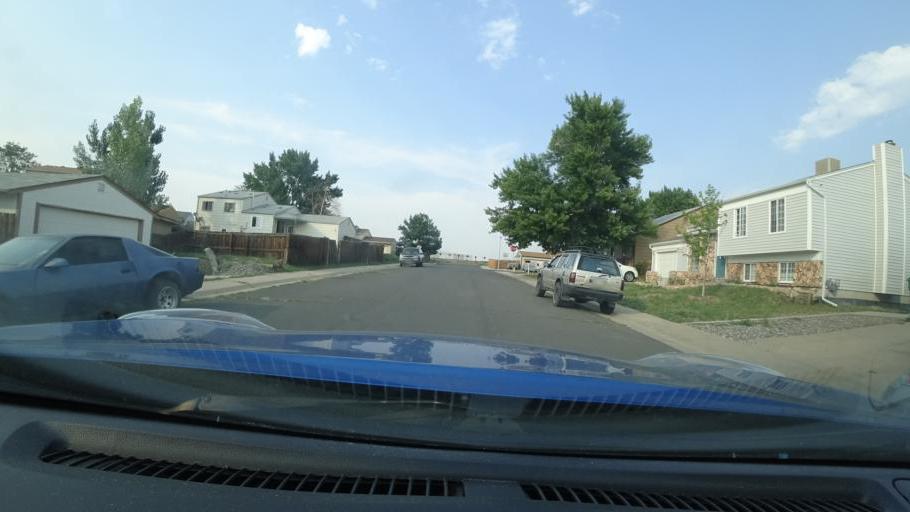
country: US
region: Colorado
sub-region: Adams County
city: Aurora
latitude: 39.7439
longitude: -104.7550
